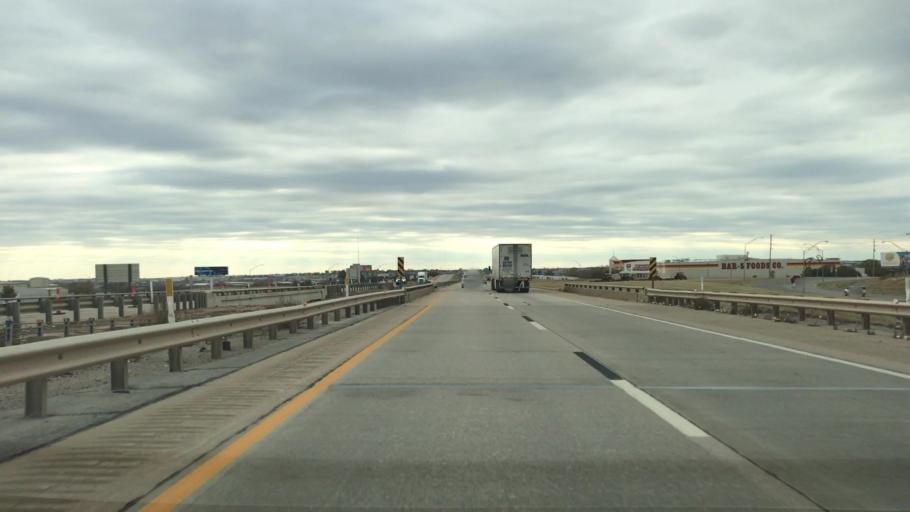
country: US
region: Oklahoma
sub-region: Beckham County
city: Elk City
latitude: 35.4085
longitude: -99.3825
